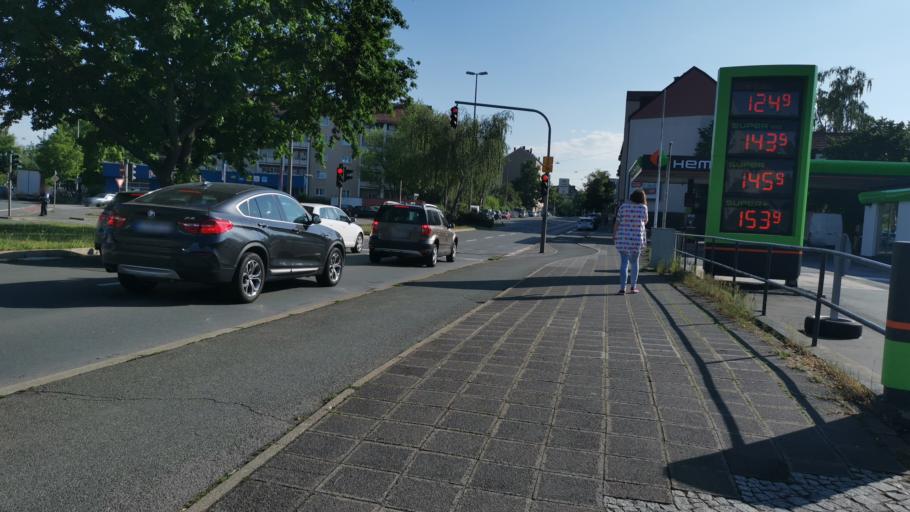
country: DE
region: Bavaria
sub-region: Regierungsbezirk Mittelfranken
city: Grossreuth bei Schweinau
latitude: 49.4254
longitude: 11.0401
